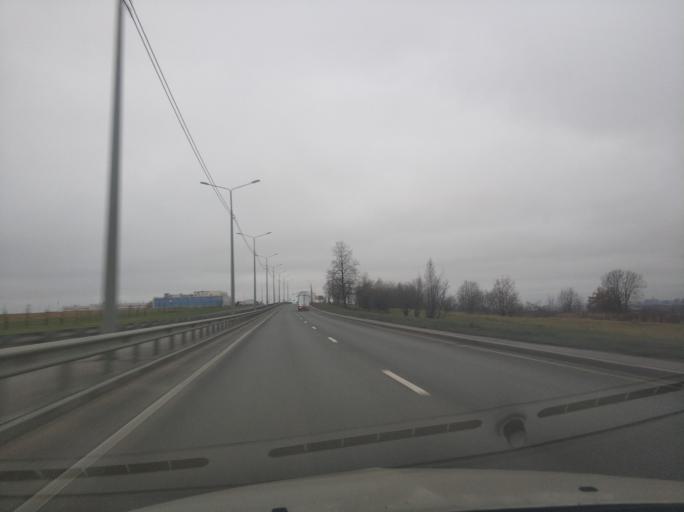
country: RU
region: St.-Petersburg
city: Pushkin
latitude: 59.7579
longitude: 30.3766
